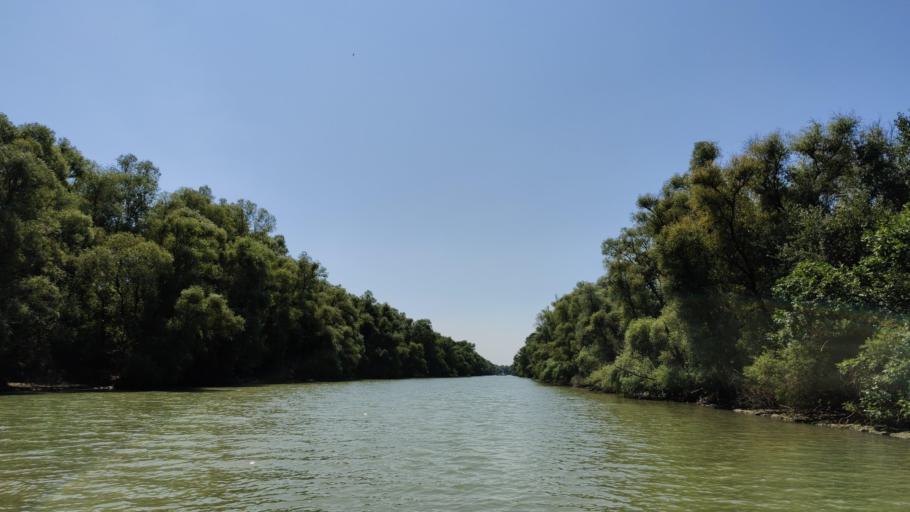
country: RO
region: Tulcea
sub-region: Comuna Pardina
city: Pardina
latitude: 45.2509
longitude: 28.9252
